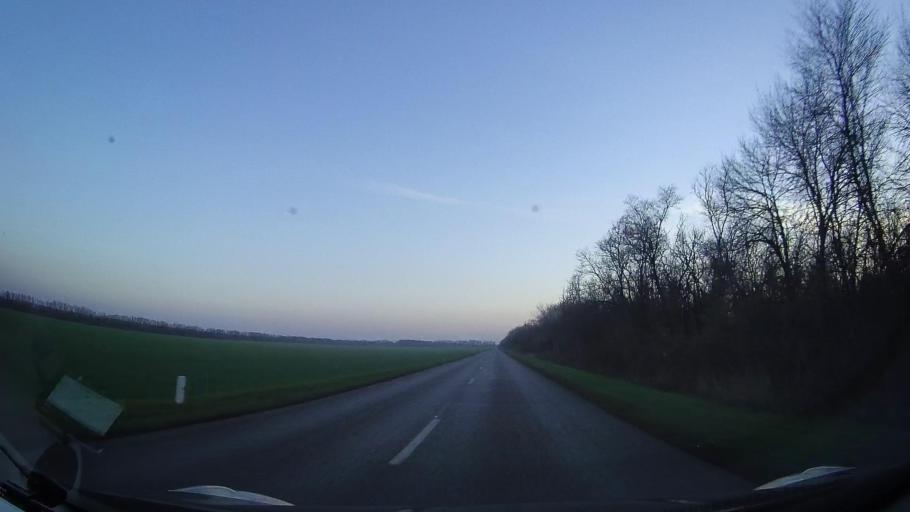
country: RU
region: Rostov
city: Zernograd
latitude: 46.9779
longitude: 40.3914
